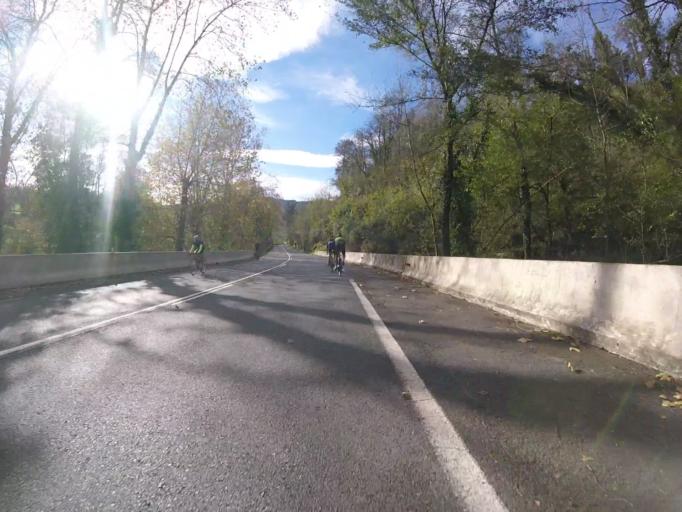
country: ES
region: Basque Country
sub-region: Provincia de Guipuzcoa
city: Usurbil
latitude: 43.2765
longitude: -2.0673
